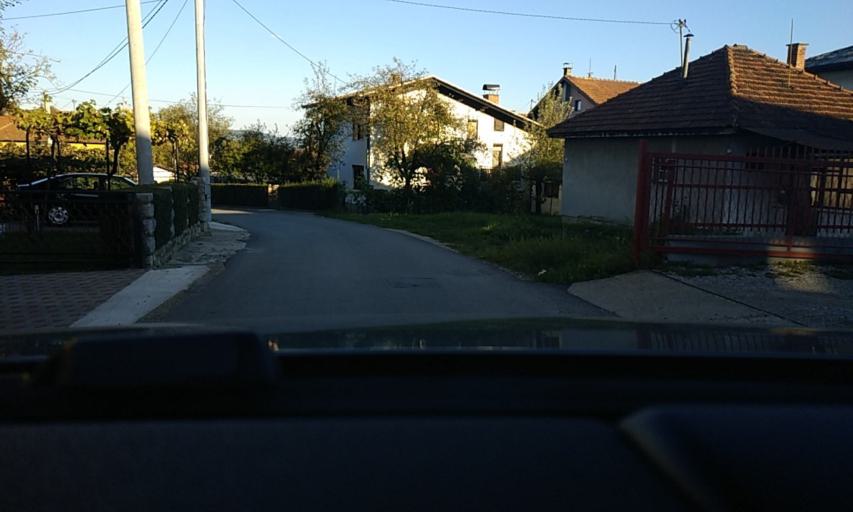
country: BA
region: Republika Srpska
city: Banja Luka
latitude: 44.7850
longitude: 17.1854
